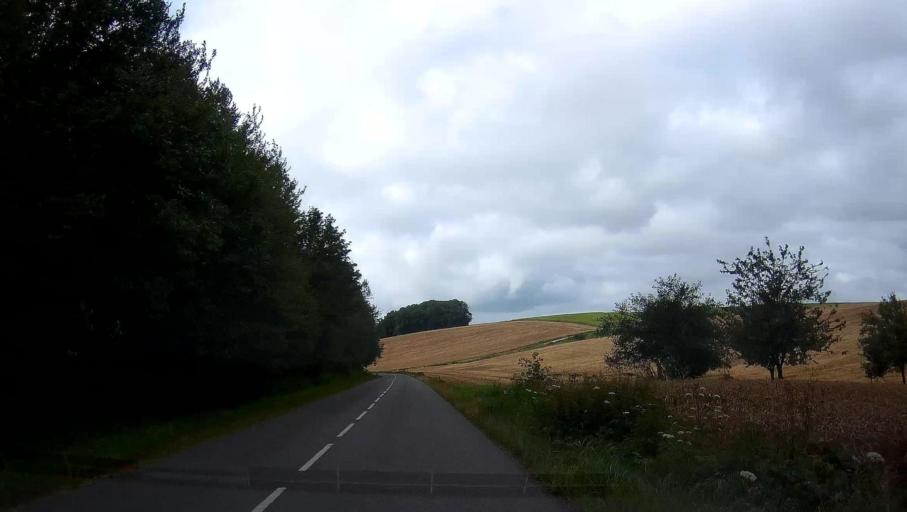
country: FR
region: Champagne-Ardenne
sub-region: Departement des Ardennes
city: Chateau-Porcien
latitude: 49.6168
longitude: 4.2314
